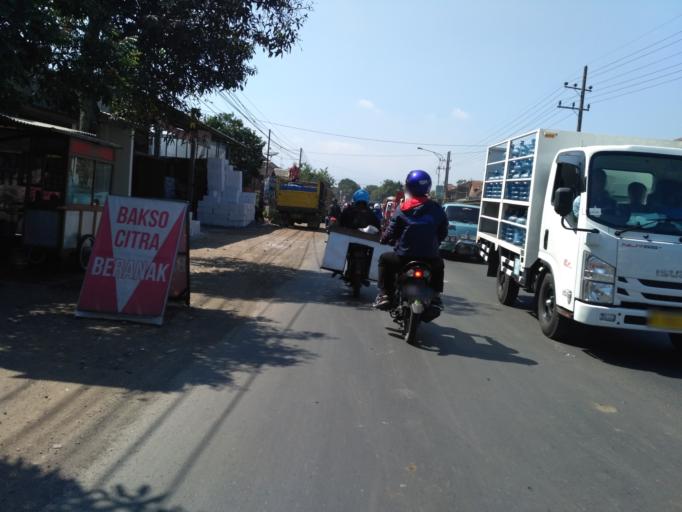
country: ID
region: East Java
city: Tamiajeng
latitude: -7.9541
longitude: 112.7028
